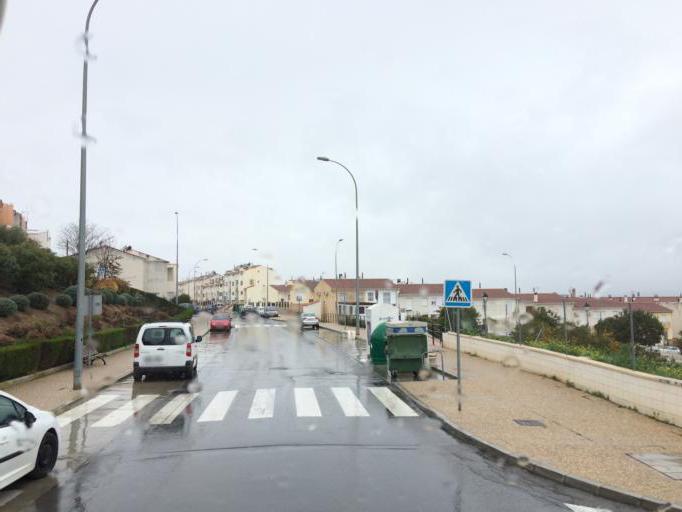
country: ES
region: Andalusia
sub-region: Provincia de Malaga
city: Antequera
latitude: 37.0258
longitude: -4.5539
